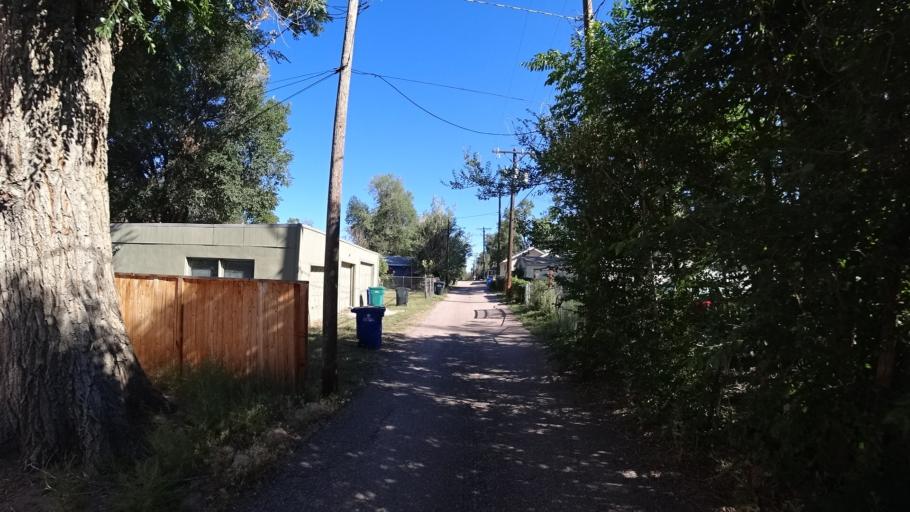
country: US
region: Colorado
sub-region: El Paso County
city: Colorado Springs
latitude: 38.8452
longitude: -104.8054
